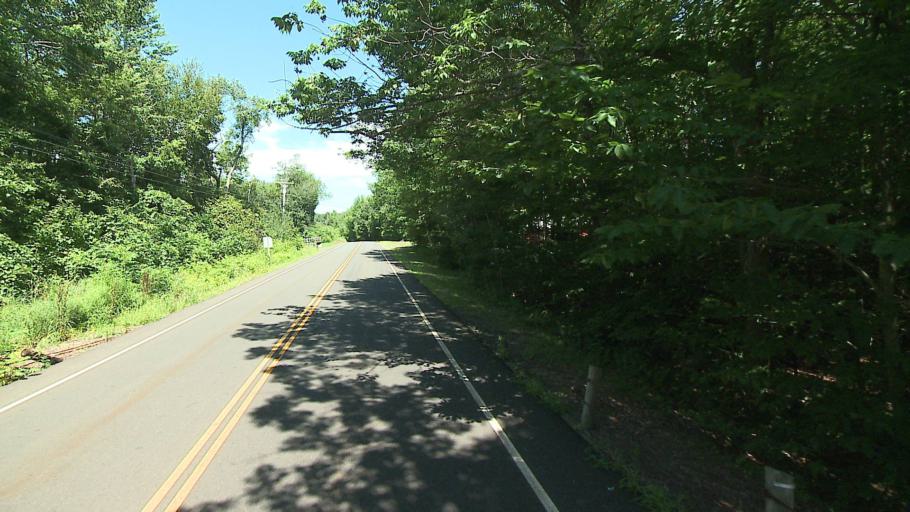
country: US
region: Connecticut
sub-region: Litchfield County
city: Winsted
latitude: 41.9933
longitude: -72.9814
